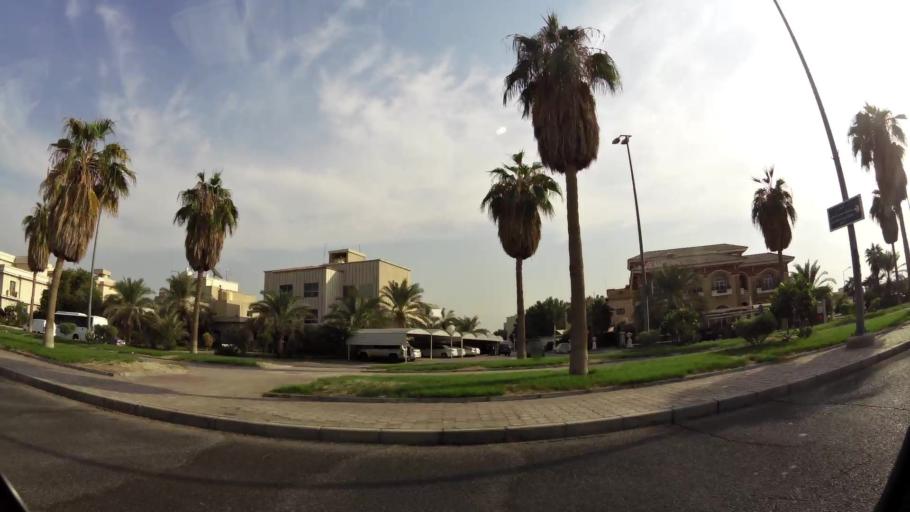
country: KW
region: Al Asimah
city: Ash Shamiyah
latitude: 29.3269
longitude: 47.9849
